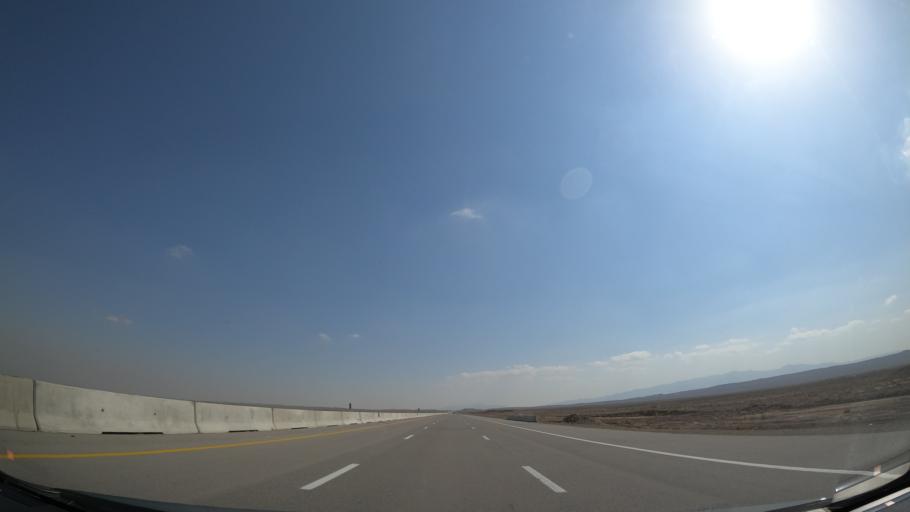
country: IR
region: Alborz
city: Nazarabad
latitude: 35.8233
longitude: 50.5105
